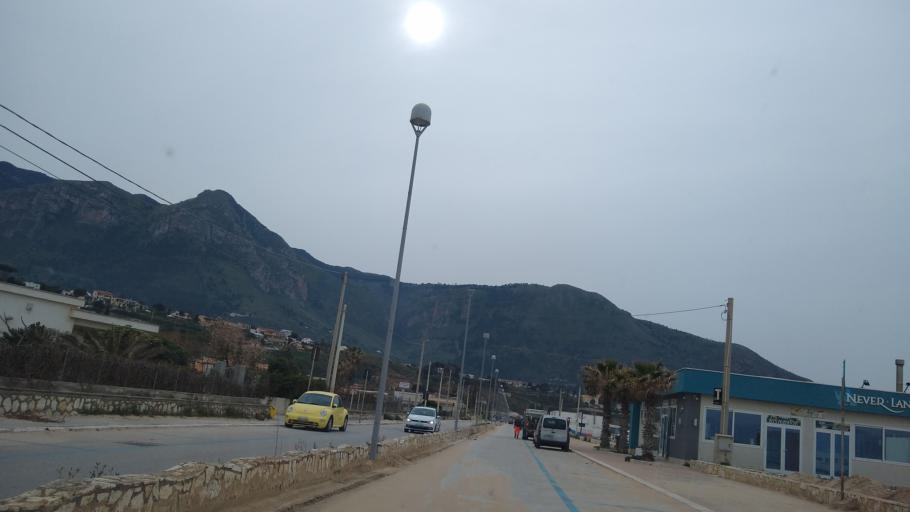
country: IT
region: Sicily
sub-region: Trapani
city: Castellammare del Golfo
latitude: 38.0237
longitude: 12.9037
